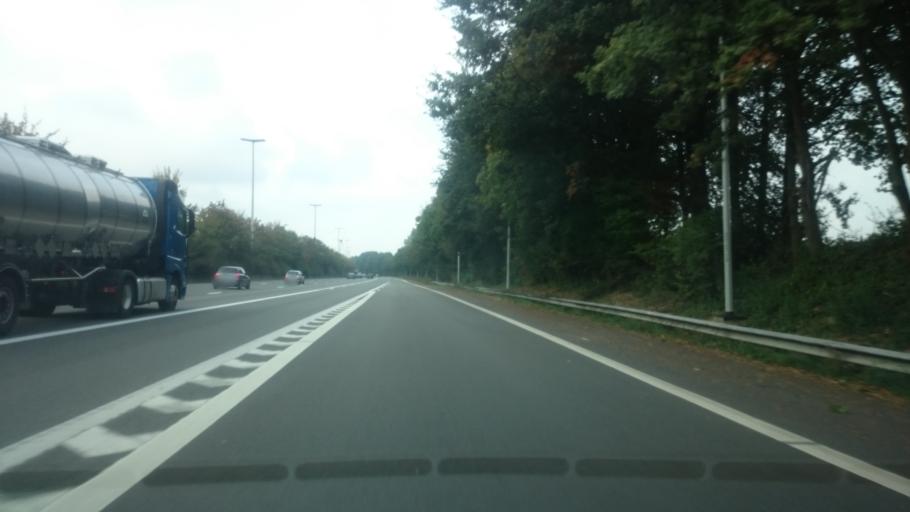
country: BE
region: Wallonia
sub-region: Province de Namur
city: Namur
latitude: 50.5245
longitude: 4.8804
